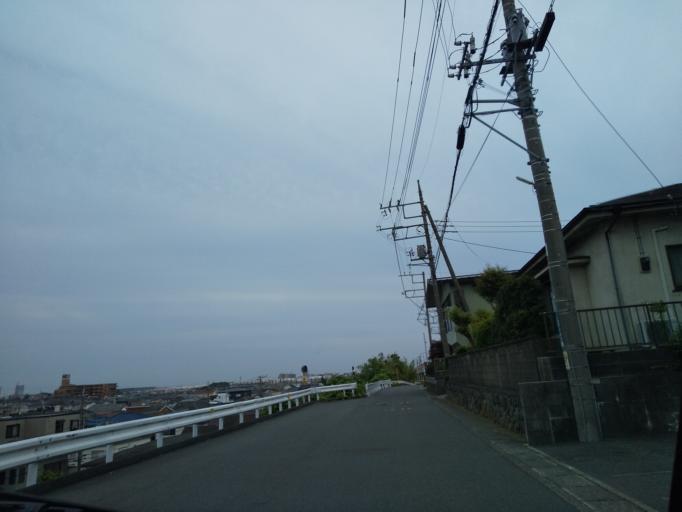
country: JP
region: Kanagawa
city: Atsugi
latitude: 35.4714
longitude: 139.3535
